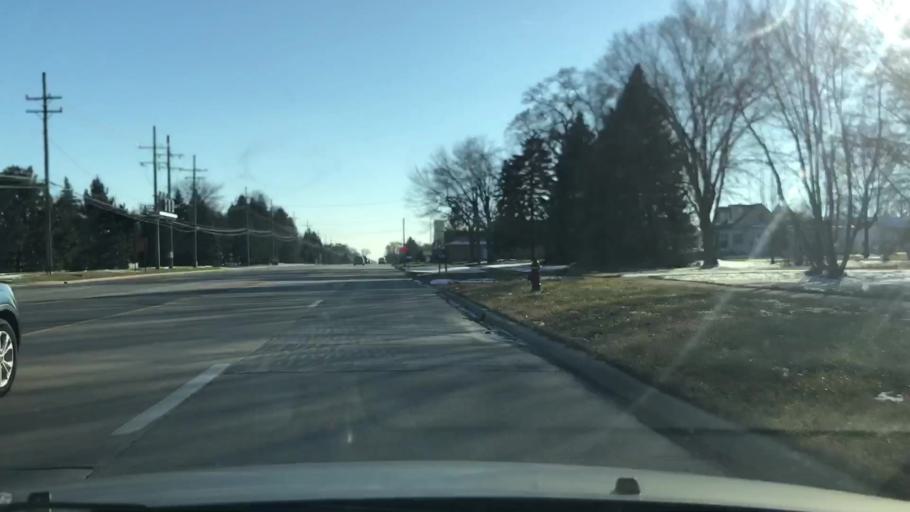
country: US
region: Michigan
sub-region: Oakland County
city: Troy
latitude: 42.5913
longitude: -83.1096
